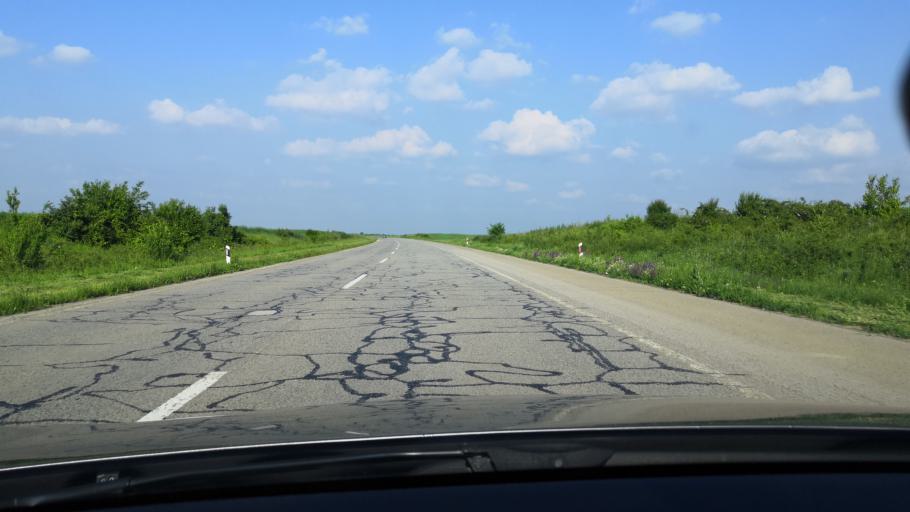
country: RS
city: Beska
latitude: 45.0905
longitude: 20.0541
